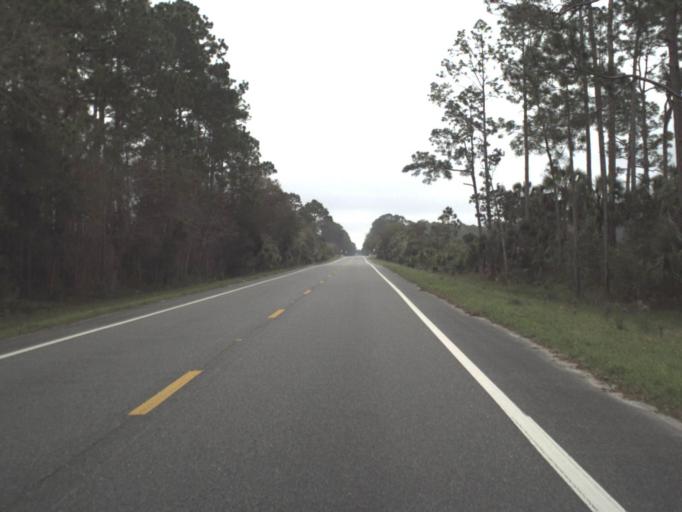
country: US
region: Florida
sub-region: Franklin County
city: Eastpoint
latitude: 29.8235
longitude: -84.8538
